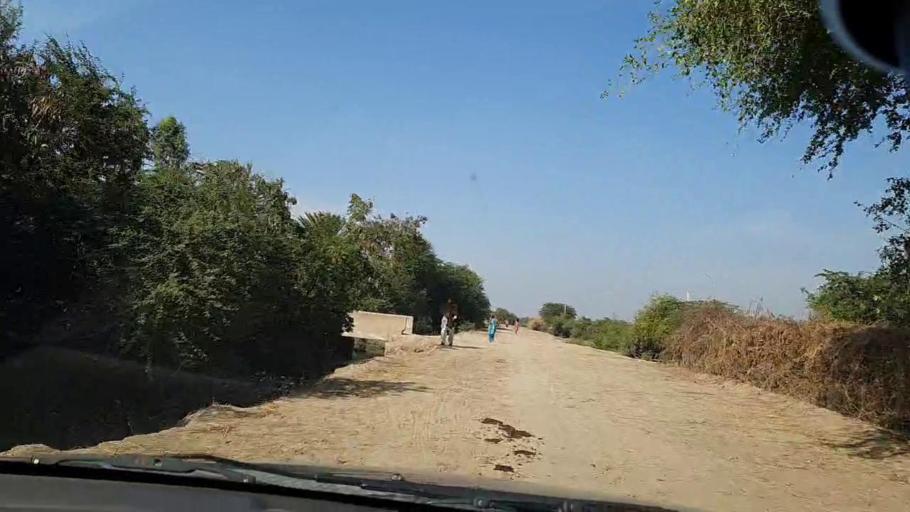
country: PK
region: Sindh
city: Mirpur Batoro
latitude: 24.6516
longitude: 68.2544
